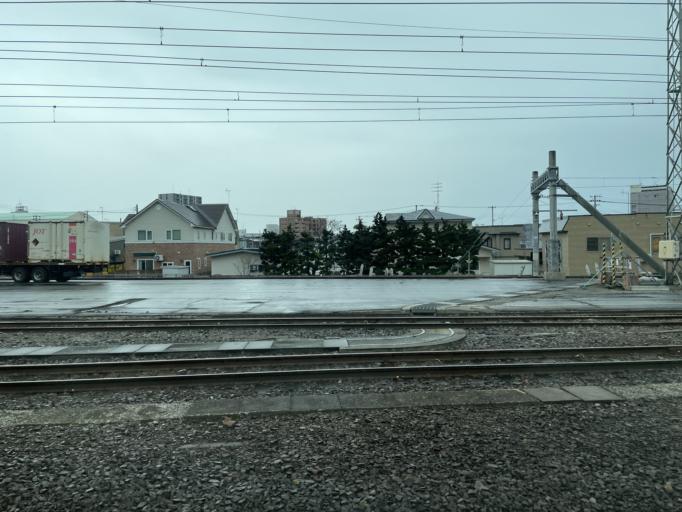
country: JP
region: Aomori
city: Hirosaki
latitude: 40.6034
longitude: 140.4836
